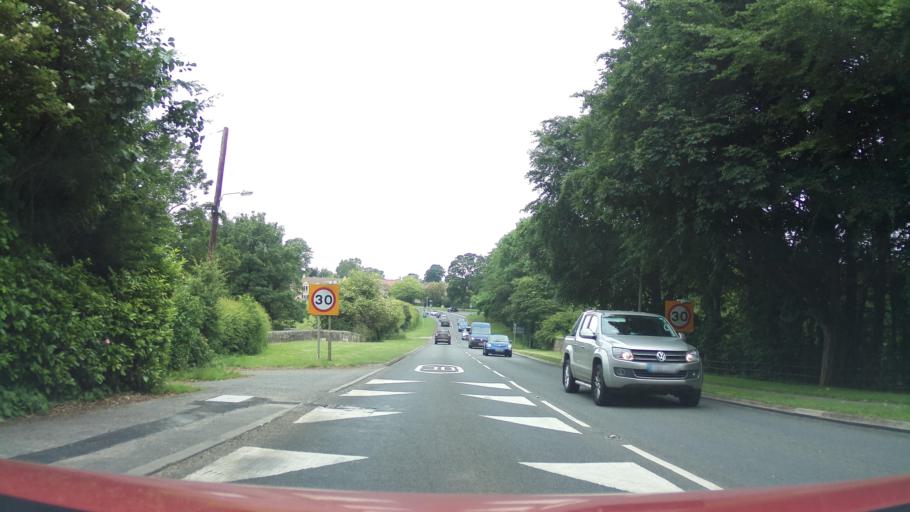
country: GB
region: England
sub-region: District of Rutland
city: Empingham
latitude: 52.6631
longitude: -0.5949
